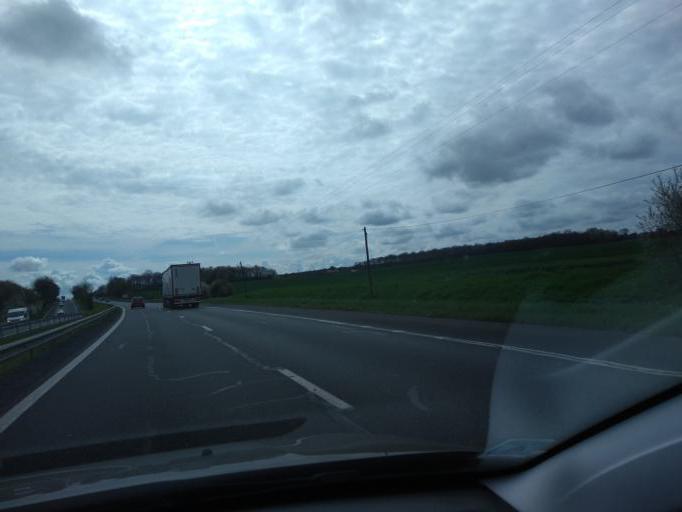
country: FR
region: Poitou-Charentes
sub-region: Departement de la Vienne
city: Iteuil
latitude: 46.4911
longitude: 0.2744
